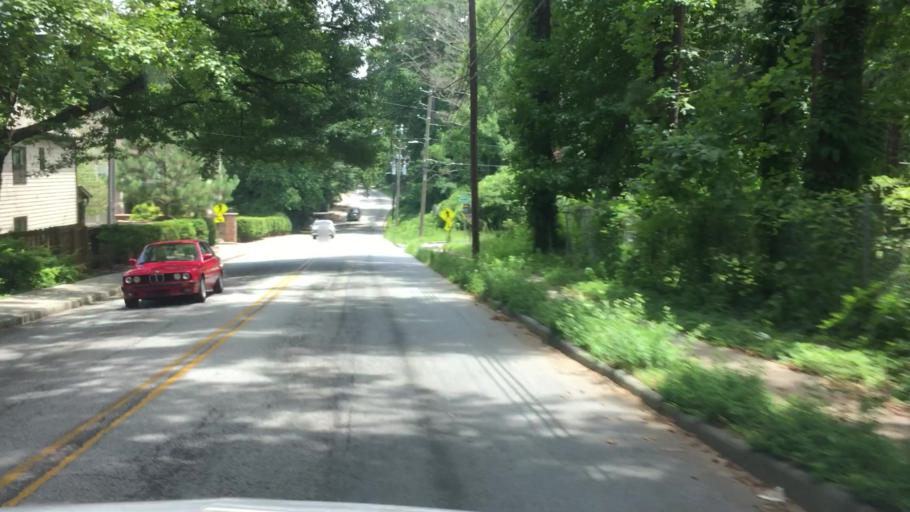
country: US
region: Georgia
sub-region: DeKalb County
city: Gresham Park
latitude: 33.7158
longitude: -84.3537
